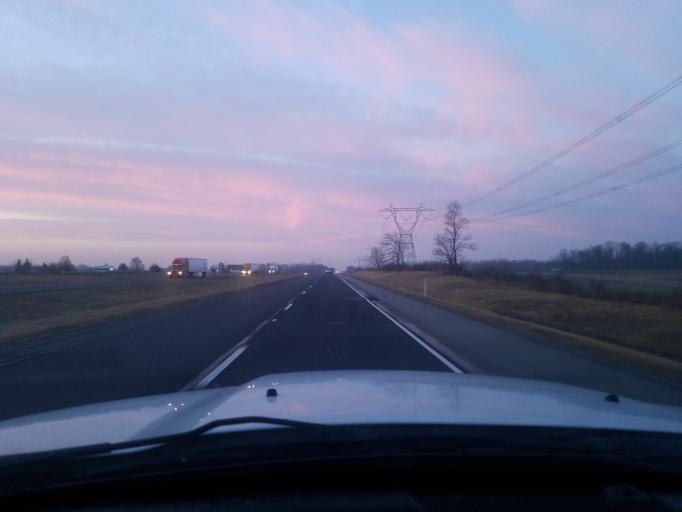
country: US
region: Indiana
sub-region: Huntington County
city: Roanoke
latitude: 40.9278
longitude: -85.3168
